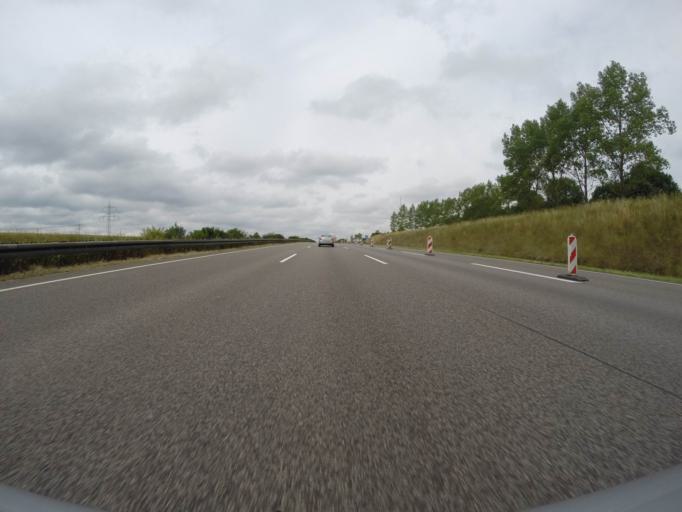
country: DE
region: Thuringia
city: Oettern
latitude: 50.9379
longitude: 11.3600
